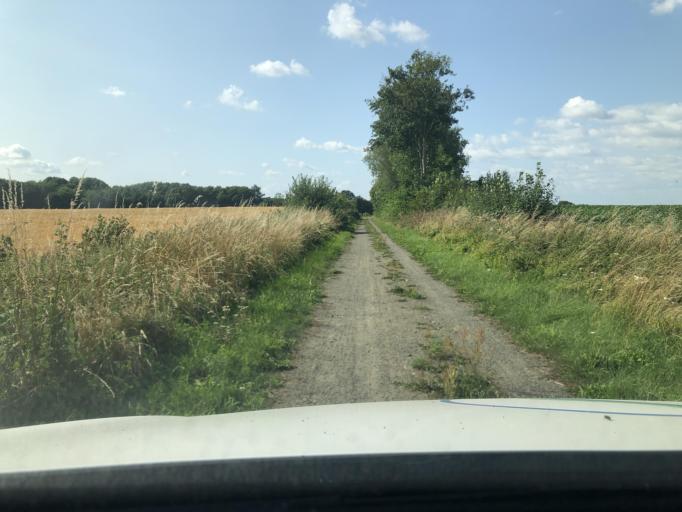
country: SE
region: Skane
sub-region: Kristianstads Kommun
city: Degeberga
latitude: 55.7985
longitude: 14.1533
